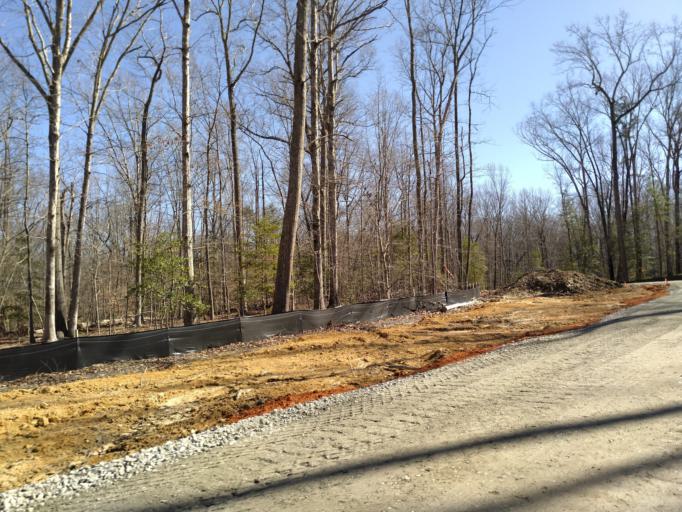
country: US
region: Virginia
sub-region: Chesterfield County
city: Chesterfield
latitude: 37.3818
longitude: -77.5586
